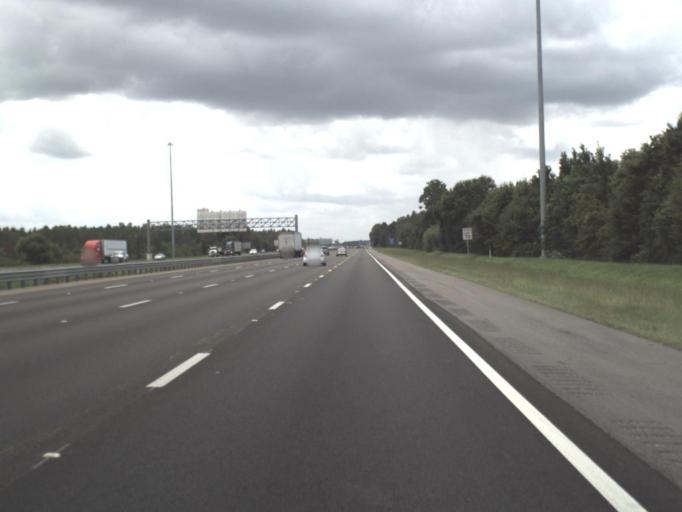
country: US
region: Florida
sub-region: Pasco County
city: Wesley Chapel
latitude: 28.2295
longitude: -82.3603
